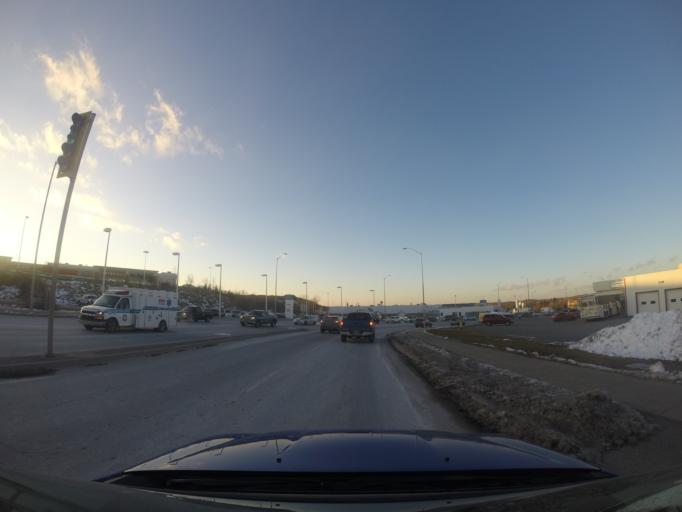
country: CA
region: Ontario
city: Greater Sudbury
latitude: 46.5042
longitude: -80.9381
